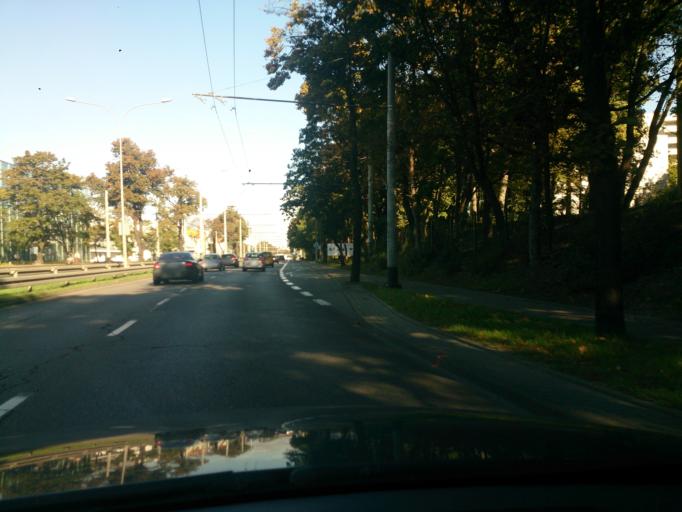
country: PL
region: Pomeranian Voivodeship
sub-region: Gdynia
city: Gdynia
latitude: 54.4942
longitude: 18.5395
